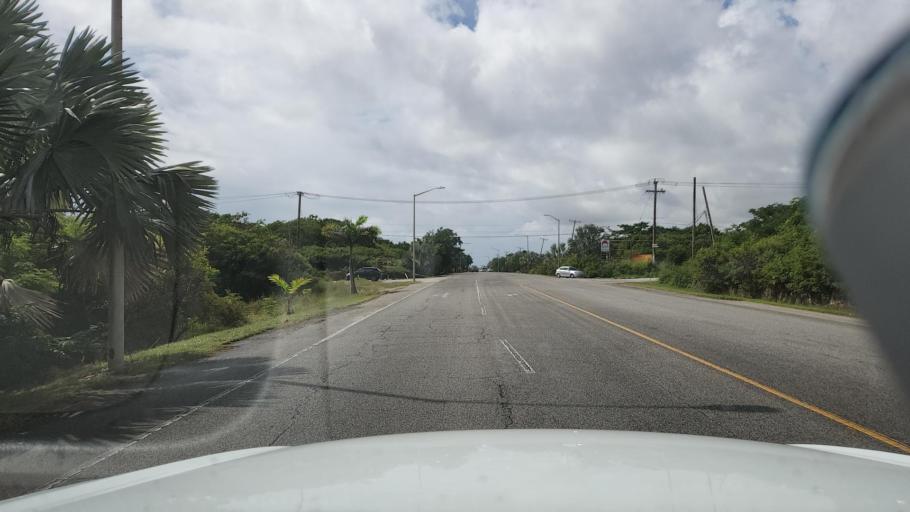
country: BB
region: Christ Church
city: Oistins
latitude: 13.0804
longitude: -59.5142
